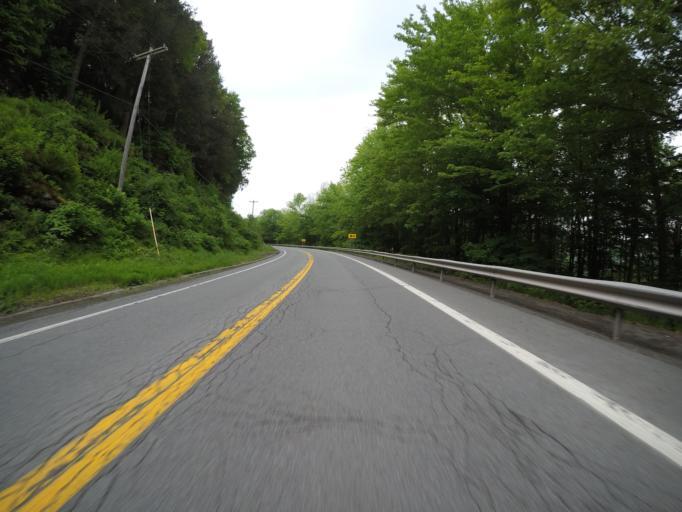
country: US
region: New York
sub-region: Delaware County
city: Delhi
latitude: 42.0808
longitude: -74.9335
